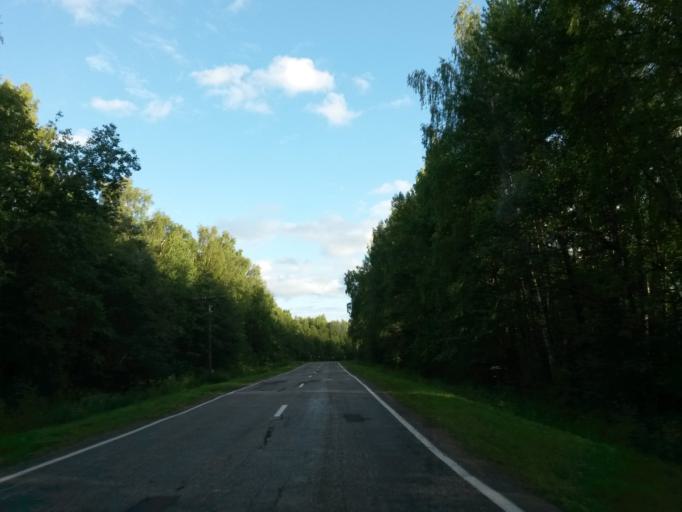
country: RU
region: Jaroslavl
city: Tutayev
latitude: 57.9196
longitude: 39.5141
